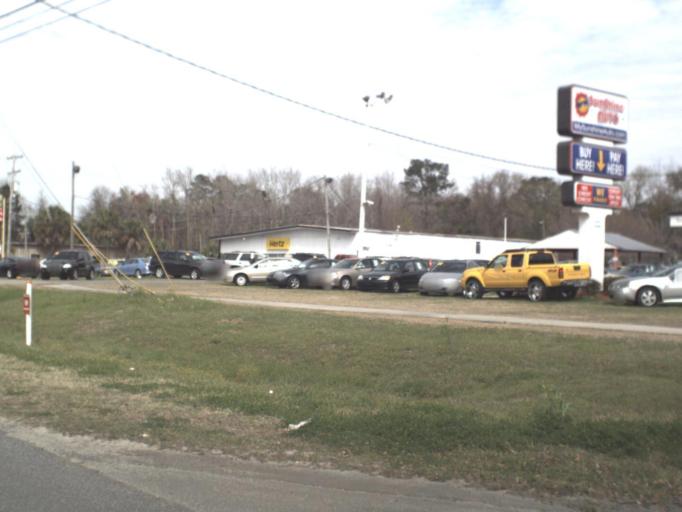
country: US
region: Florida
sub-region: Leon County
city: Tallahassee
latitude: 30.4587
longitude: -84.3510
